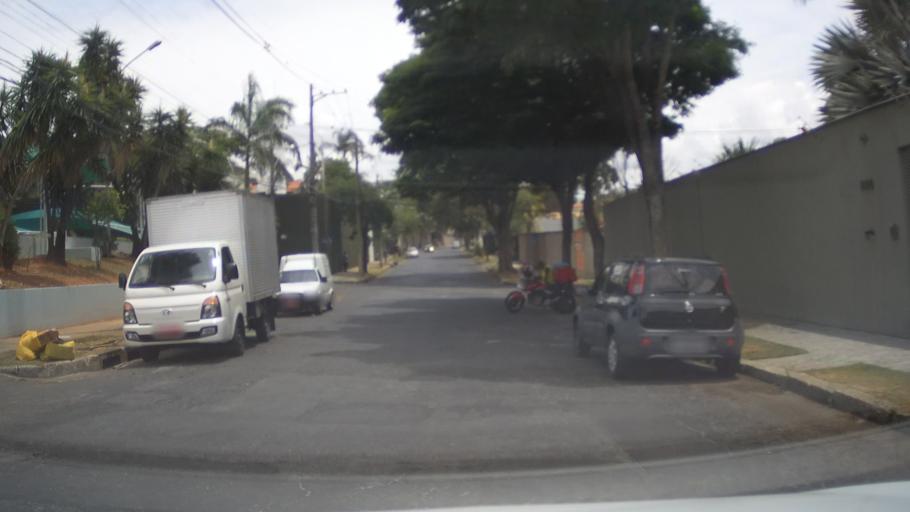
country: BR
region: Minas Gerais
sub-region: Belo Horizonte
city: Belo Horizonte
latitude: -19.8568
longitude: -43.9688
